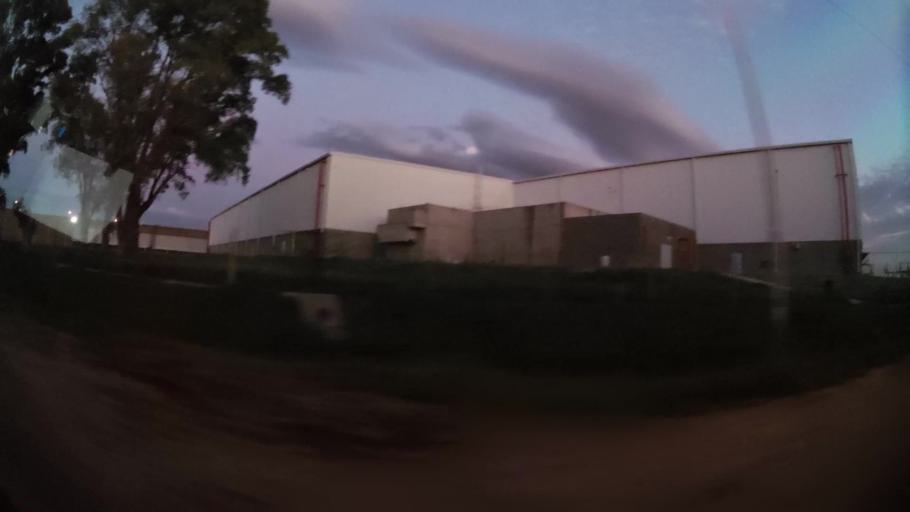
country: AR
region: Buenos Aires
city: Santa Catalina - Dique Lujan
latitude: -34.4612
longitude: -58.7439
